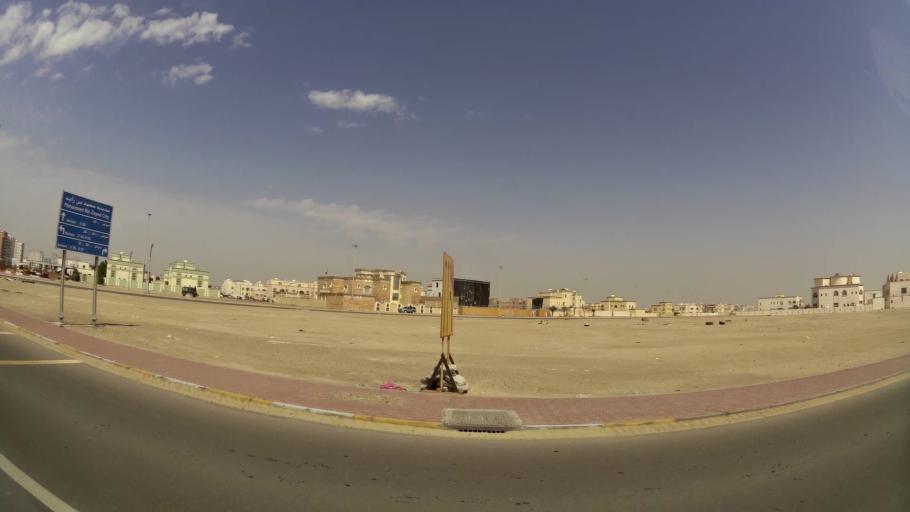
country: AE
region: Abu Dhabi
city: Abu Dhabi
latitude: 24.3144
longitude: 54.5407
